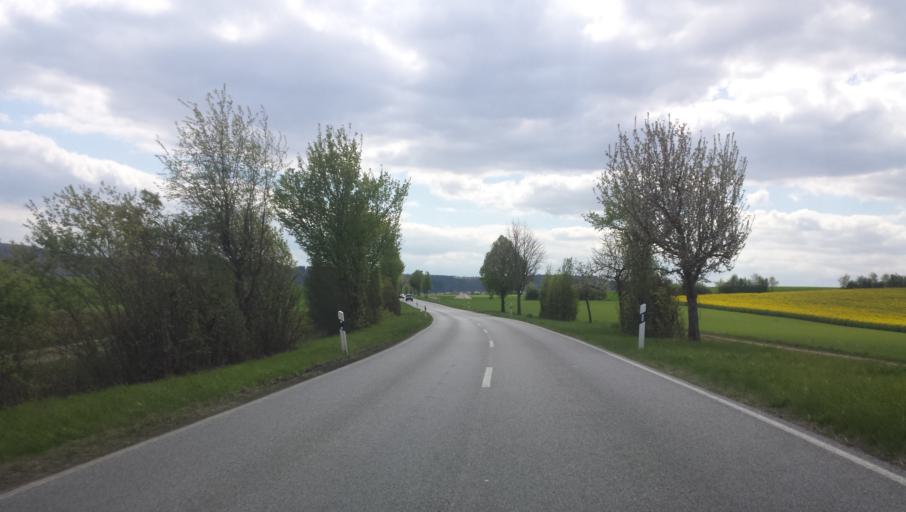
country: DE
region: Baden-Wuerttemberg
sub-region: Regierungsbezirk Stuttgart
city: Eppingen
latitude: 49.1172
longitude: 8.8977
